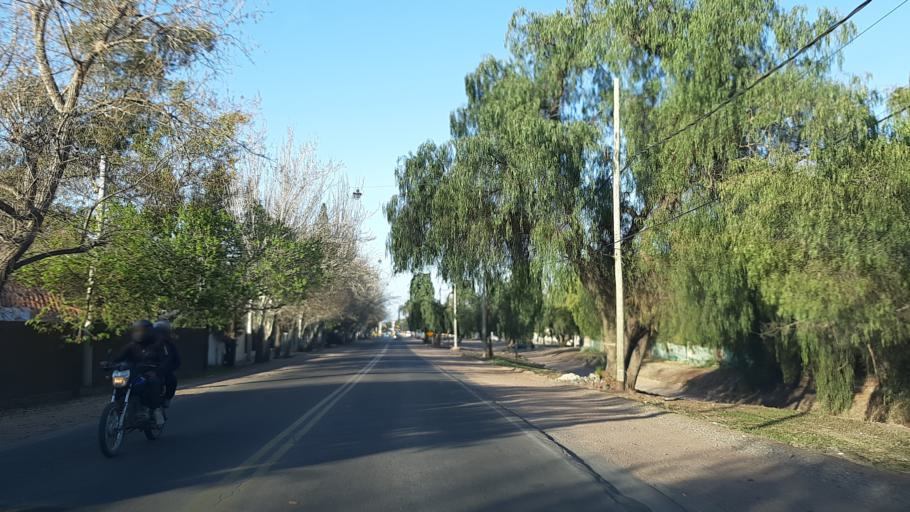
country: AR
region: Mendoza
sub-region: Departamento de Godoy Cruz
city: Godoy Cruz
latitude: -32.9631
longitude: -68.8696
